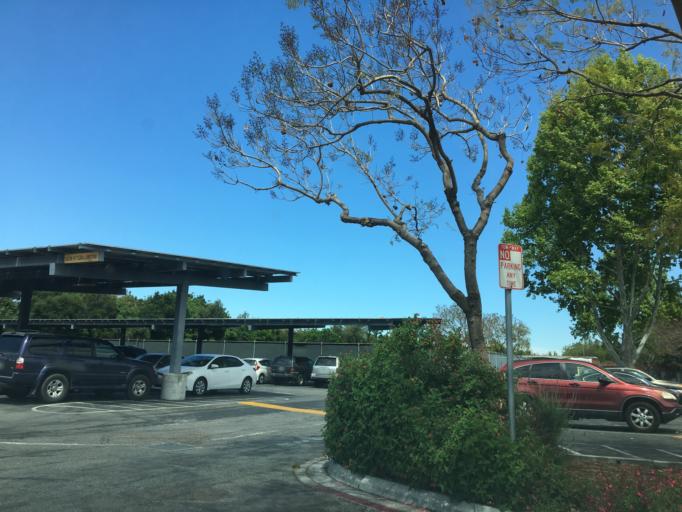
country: US
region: California
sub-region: Santa Clara County
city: San Jose
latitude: 37.3513
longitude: -121.8726
